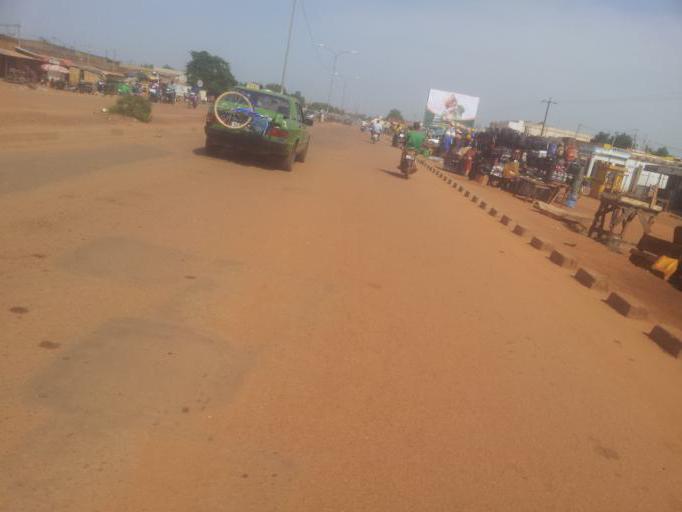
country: BF
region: Centre
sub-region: Kadiogo Province
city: Ouagadougou
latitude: 12.3894
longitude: -1.5753
